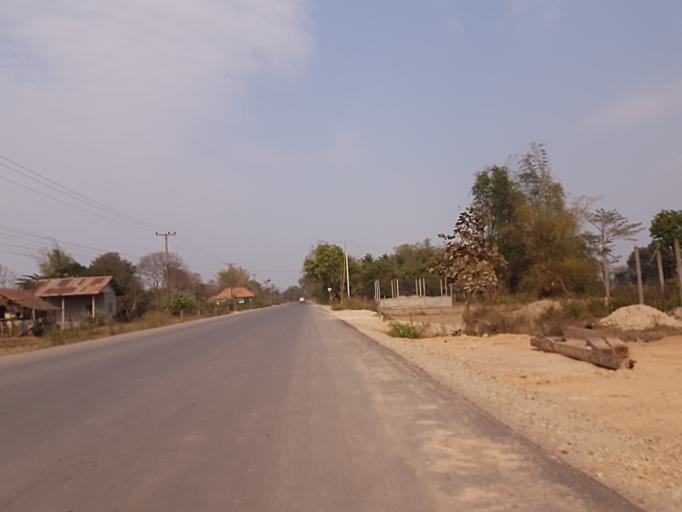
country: TH
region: Nong Khai
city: Nong Khai
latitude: 17.9592
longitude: 102.8320
